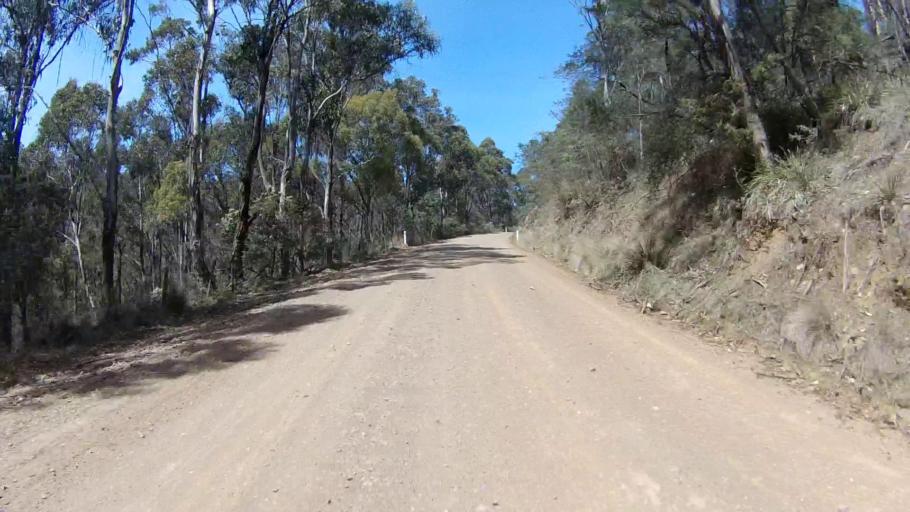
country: AU
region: Tasmania
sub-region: Sorell
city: Sorell
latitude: -42.6518
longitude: 147.7436
